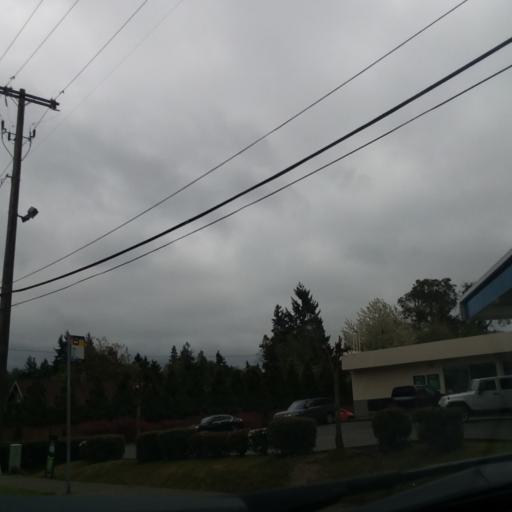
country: US
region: Washington
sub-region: King County
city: Boulevard Park
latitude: 47.5030
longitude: -122.3229
